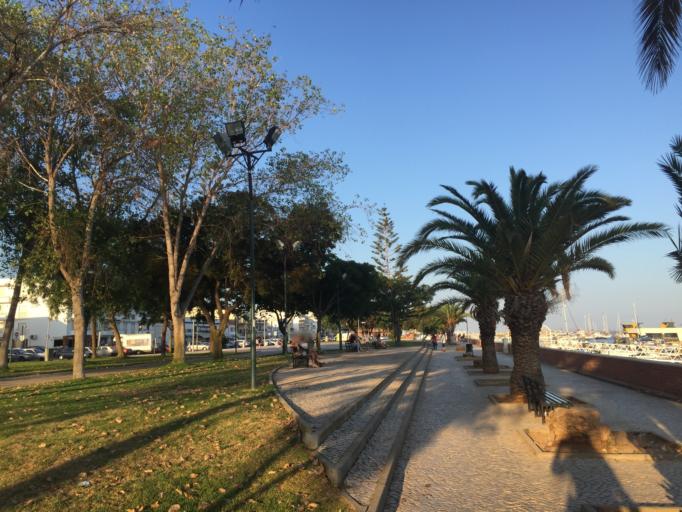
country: PT
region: Faro
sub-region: Olhao
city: Olhao
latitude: 37.0233
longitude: -7.8448
